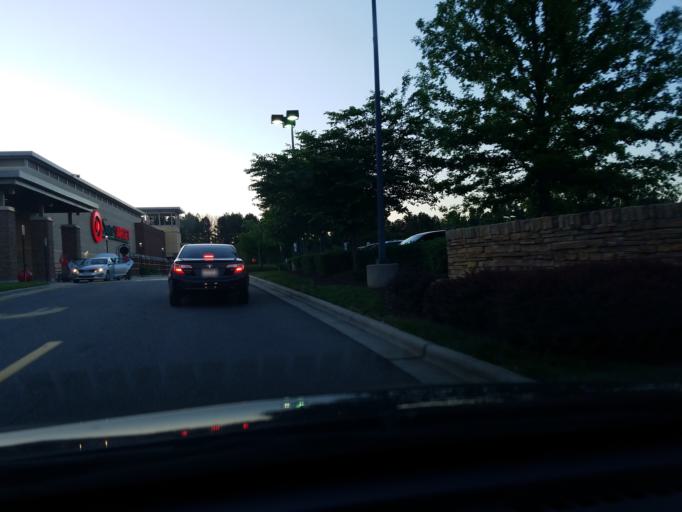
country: US
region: North Carolina
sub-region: Orange County
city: Chapel Hill
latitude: 35.9024
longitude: -78.9555
